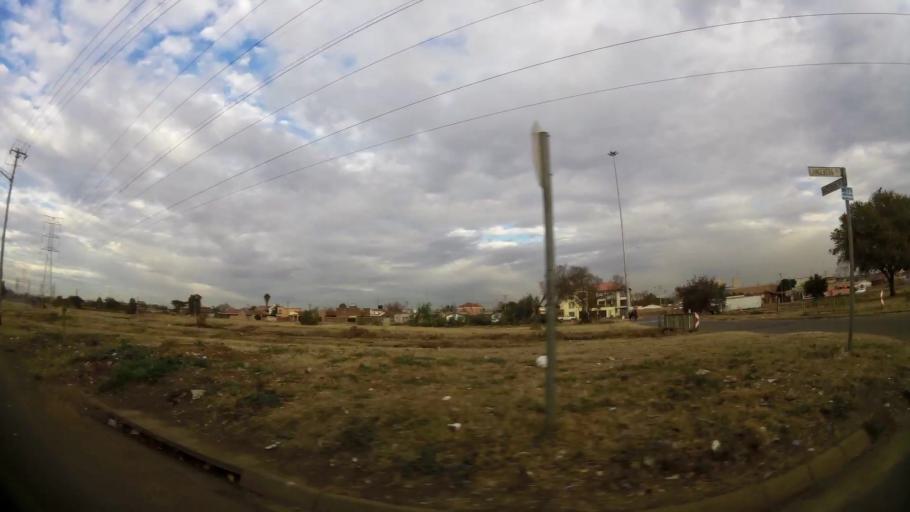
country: ZA
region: Gauteng
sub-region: City of Tshwane Metropolitan Municipality
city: Pretoria
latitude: -25.7142
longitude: 28.3248
